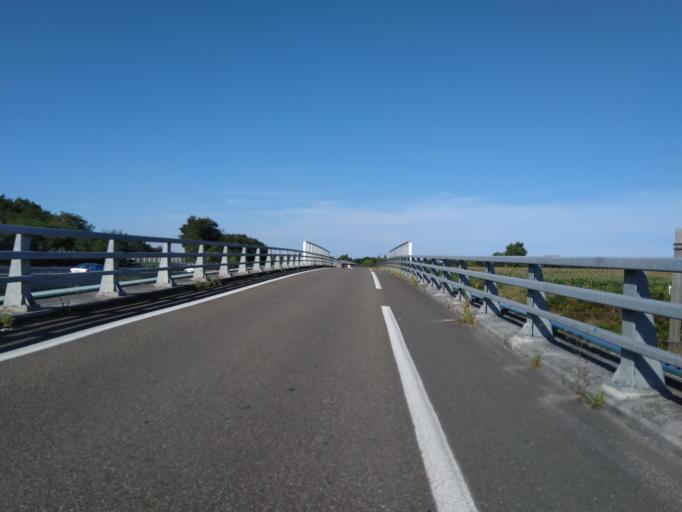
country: FR
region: Aquitaine
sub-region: Departement des Landes
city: Saint-Vincent-de-Paul
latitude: 43.7378
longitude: -1.0222
